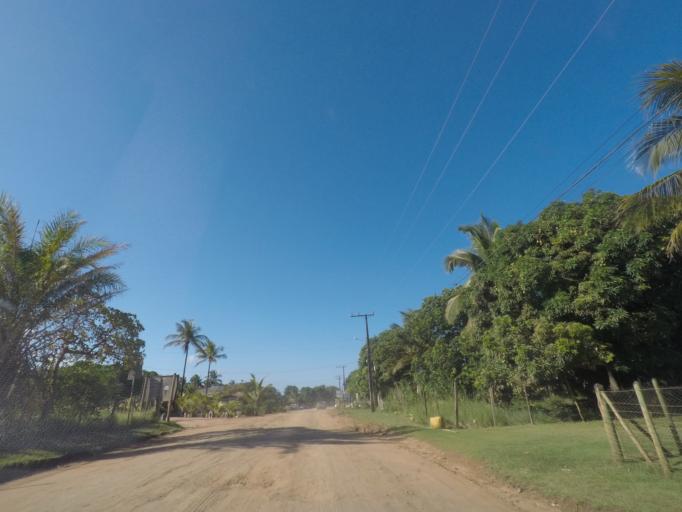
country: BR
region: Bahia
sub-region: Marau
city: Marau
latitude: -14.0444
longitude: -38.9554
